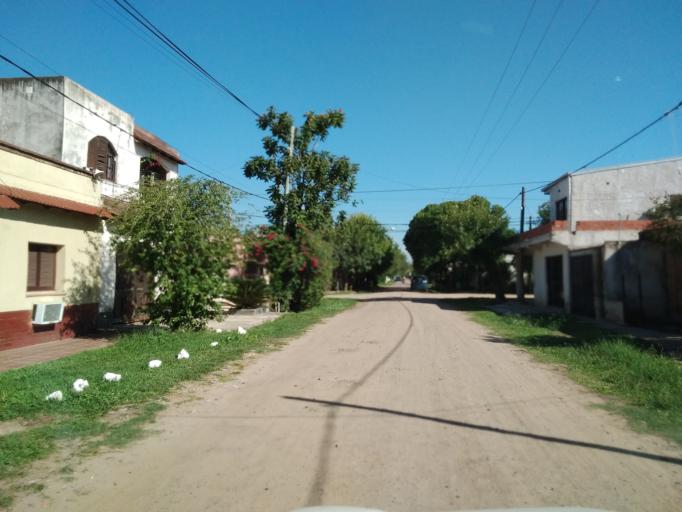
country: AR
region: Corrientes
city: Corrientes
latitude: -27.4833
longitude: -58.8057
